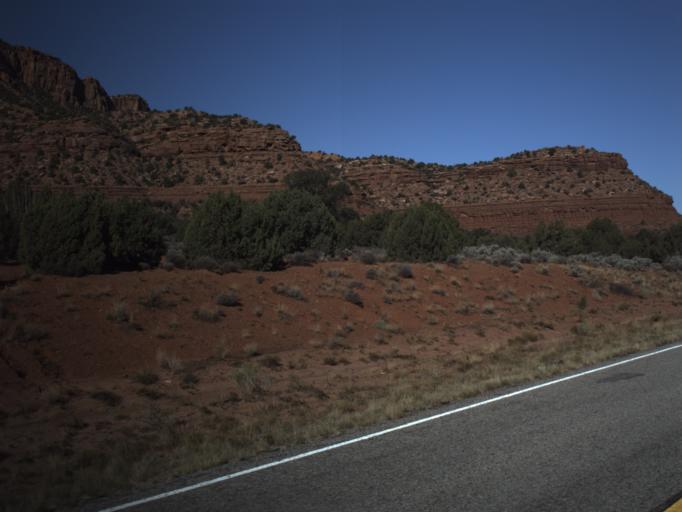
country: US
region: Utah
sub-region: San Juan County
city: Blanding
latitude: 37.6486
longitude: -110.1688
